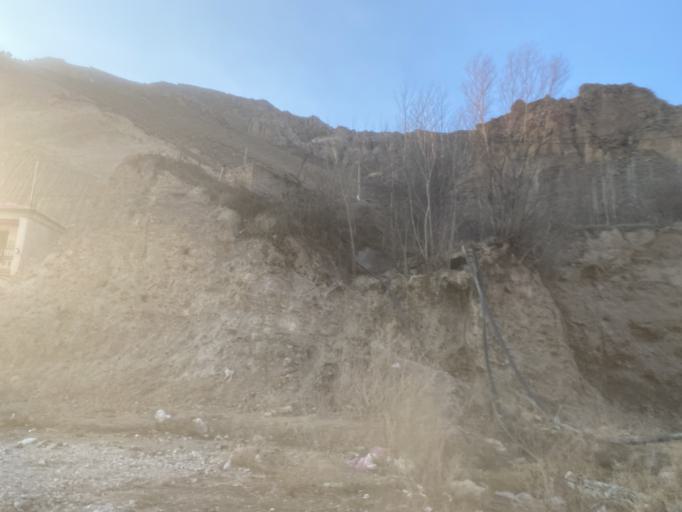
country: IR
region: Tehran
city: Damavand
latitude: 35.9015
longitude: 52.2169
